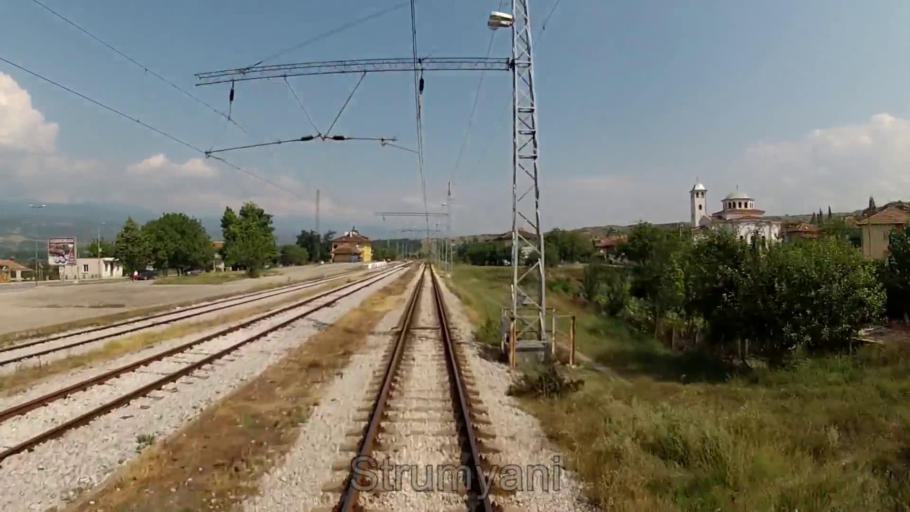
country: BG
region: Blagoevgrad
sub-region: Obshtina Strumyani
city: Strumyani
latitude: 41.6317
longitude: 23.2085
